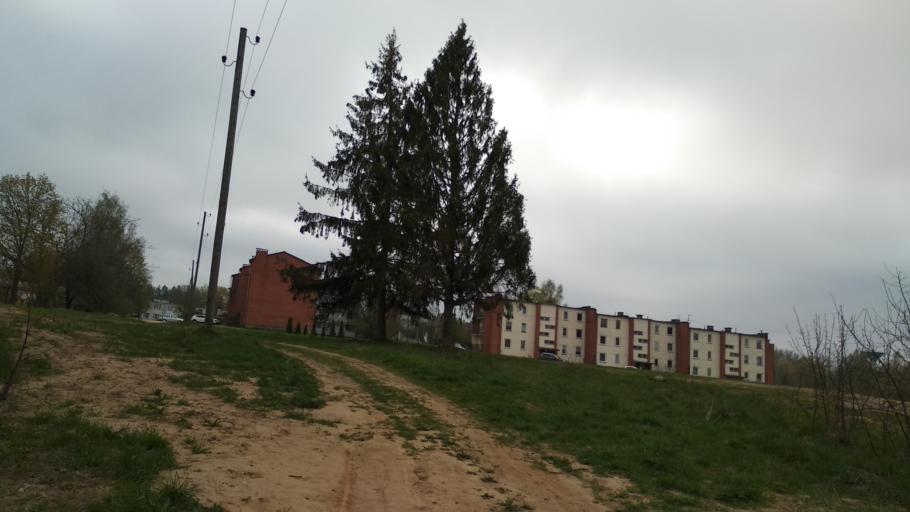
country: LV
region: Malpils
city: Malpils
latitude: 57.0137
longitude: 24.9525
